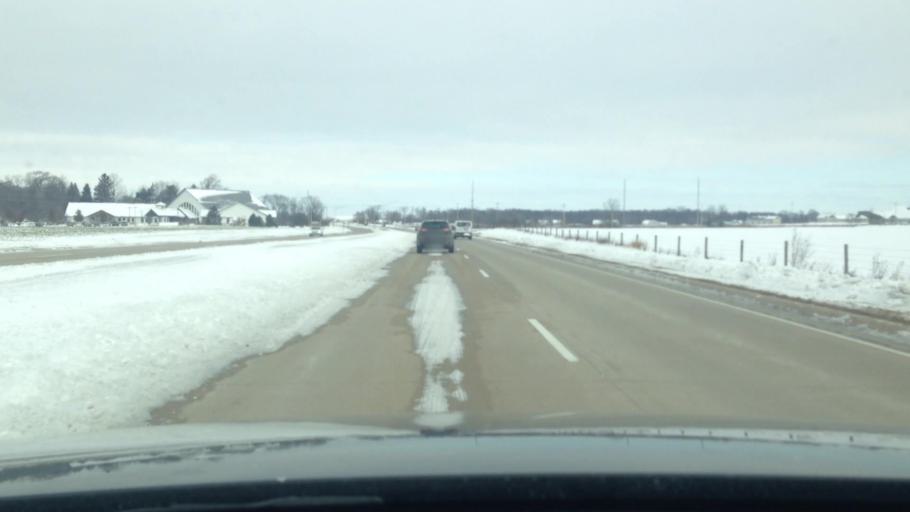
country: US
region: Wisconsin
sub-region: Walworth County
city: Lake Geneva
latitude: 42.5709
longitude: -88.4125
